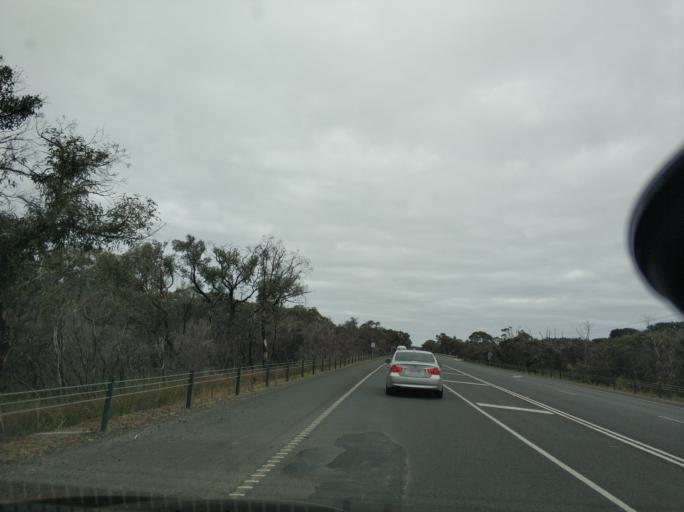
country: AU
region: Victoria
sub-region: Surf Coast
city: Anglesea
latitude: -38.3766
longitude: 144.2171
